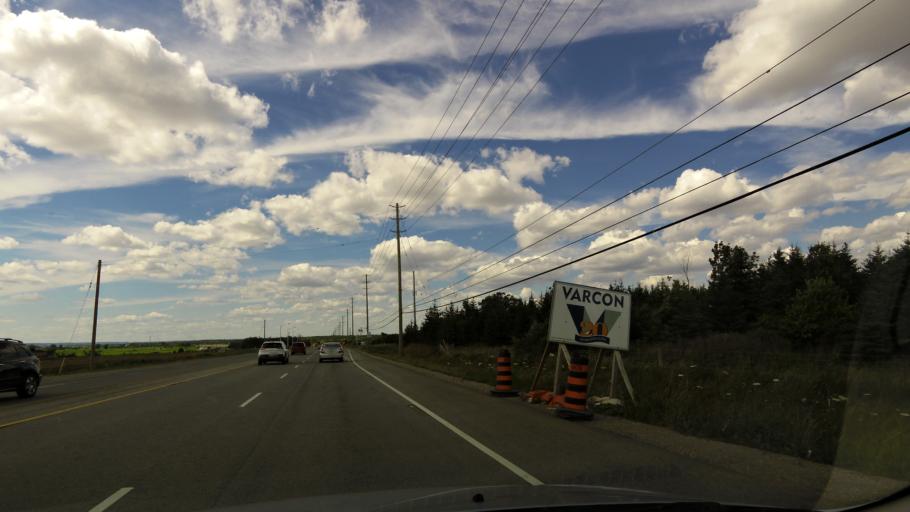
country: CA
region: Ontario
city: Burlington
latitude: 43.4600
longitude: -79.8049
